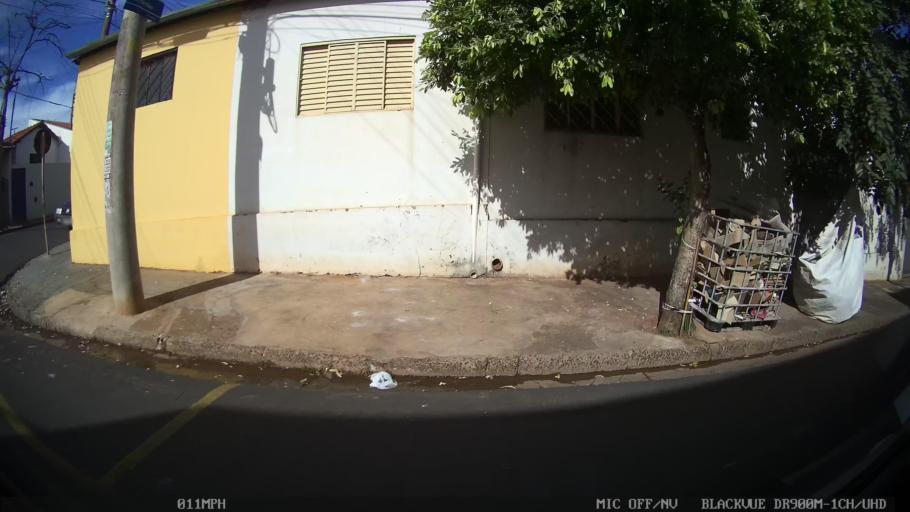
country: BR
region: Sao Paulo
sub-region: Catanduva
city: Catanduva
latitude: -21.1246
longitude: -48.9758
